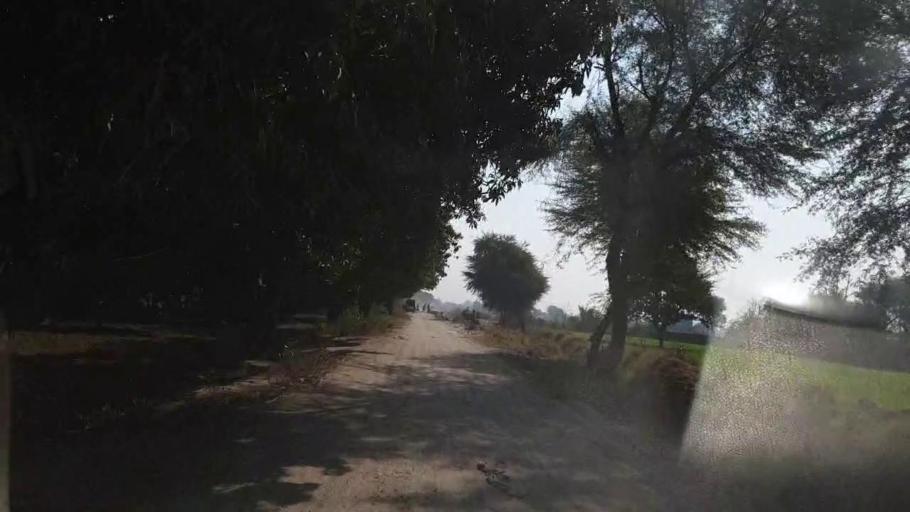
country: PK
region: Sindh
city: Matiari
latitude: 25.5129
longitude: 68.4605
